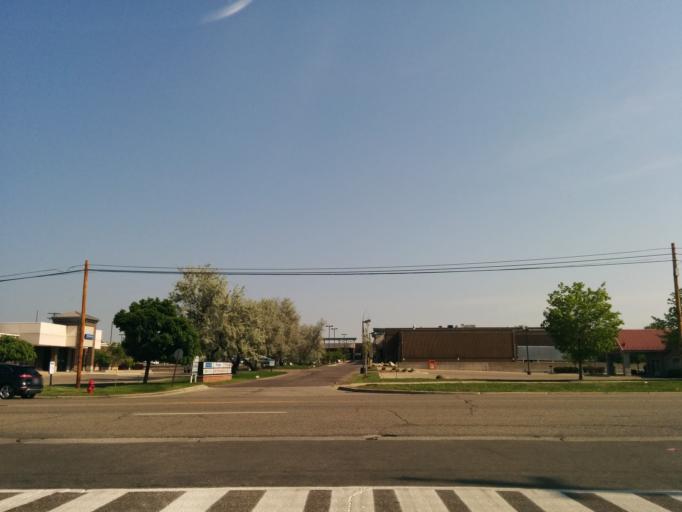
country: US
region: Michigan
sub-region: Oakland County
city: West Bloomfield Township
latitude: 42.5428
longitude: -83.3592
